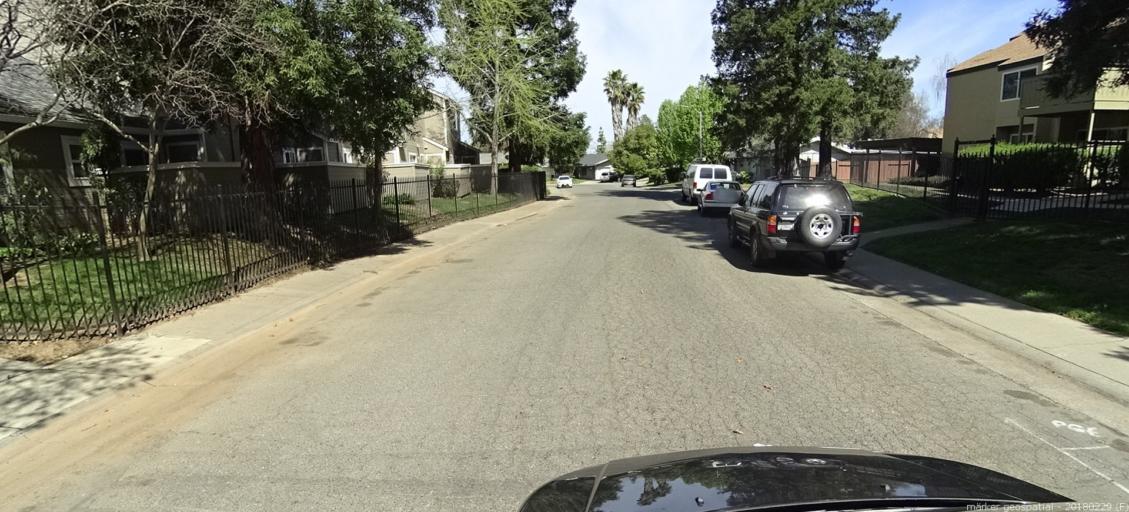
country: US
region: California
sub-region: Sacramento County
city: Rosemont
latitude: 38.5436
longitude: -121.3604
